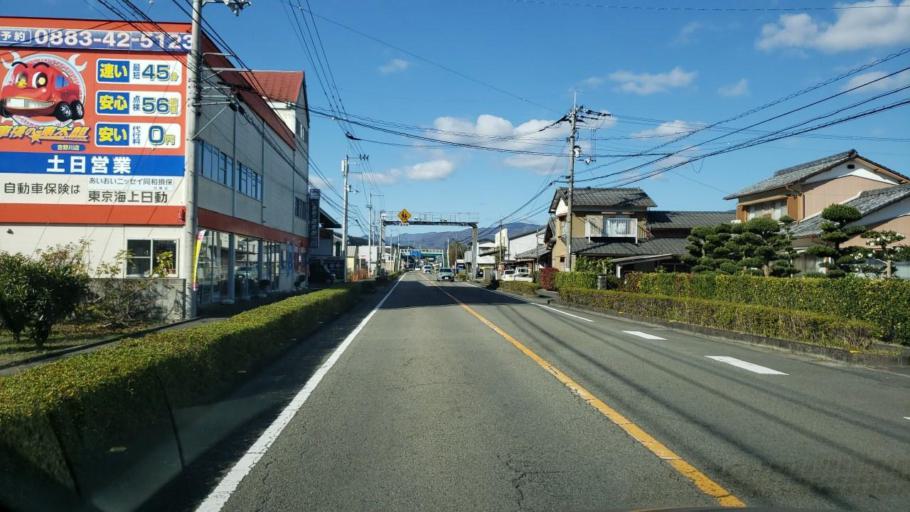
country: JP
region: Tokushima
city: Wakimachi
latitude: 34.0606
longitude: 134.2113
